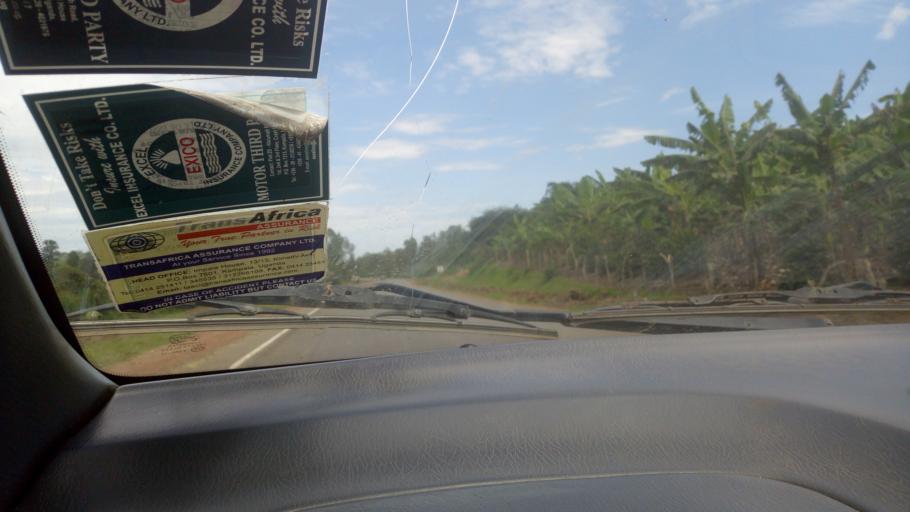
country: UG
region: Western Region
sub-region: Mbarara District
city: Bwizibwera
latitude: -0.3706
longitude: 30.5646
